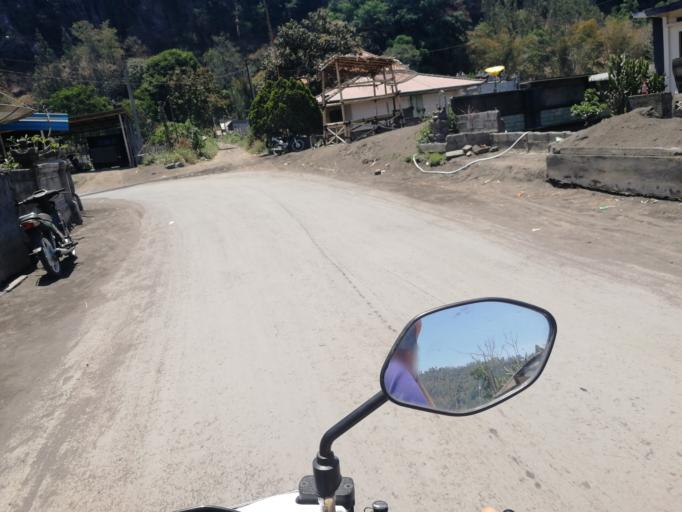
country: ID
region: Bali
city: Banjar Trunyan
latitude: -8.2238
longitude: 115.4098
